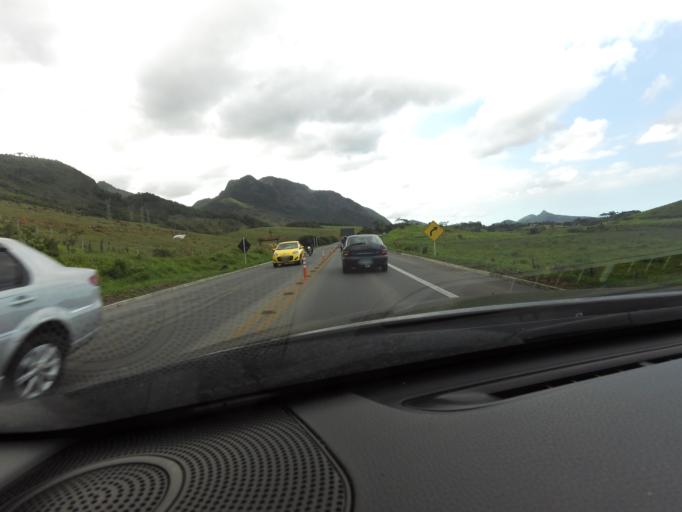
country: BR
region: Espirito Santo
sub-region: Guarapari
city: Guarapari
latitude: -20.6100
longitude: -40.5102
